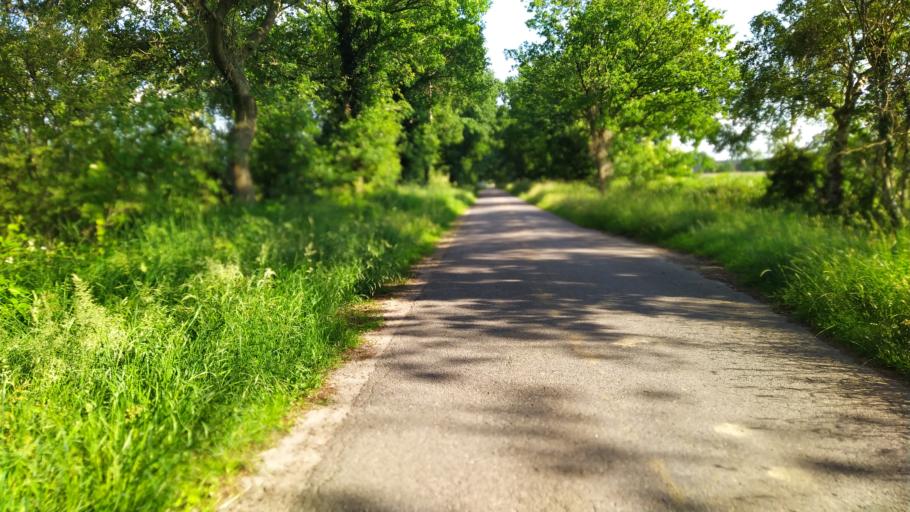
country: DE
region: Lower Saxony
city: Lintig
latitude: 53.6093
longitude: 8.8902
